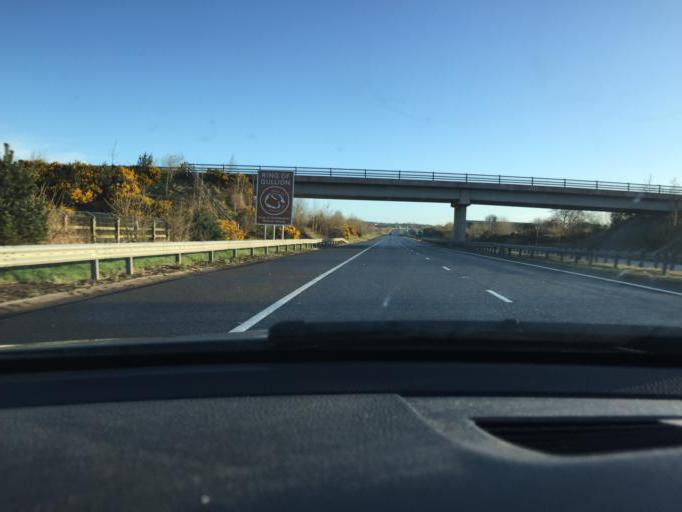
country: GB
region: Northern Ireland
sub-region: Newry and Mourne District
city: Newry
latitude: 54.1189
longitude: -6.3625
